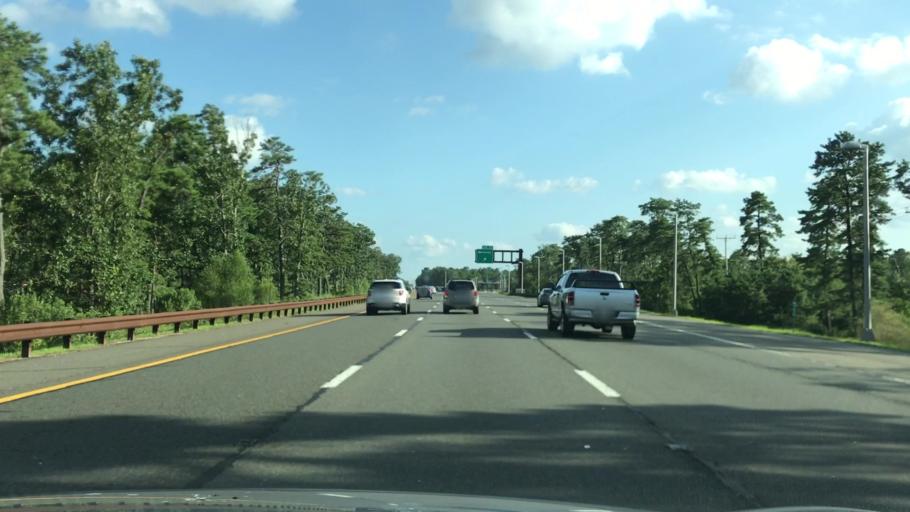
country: US
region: New Jersey
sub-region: Ocean County
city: South Toms River
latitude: 39.9109
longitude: -74.2124
